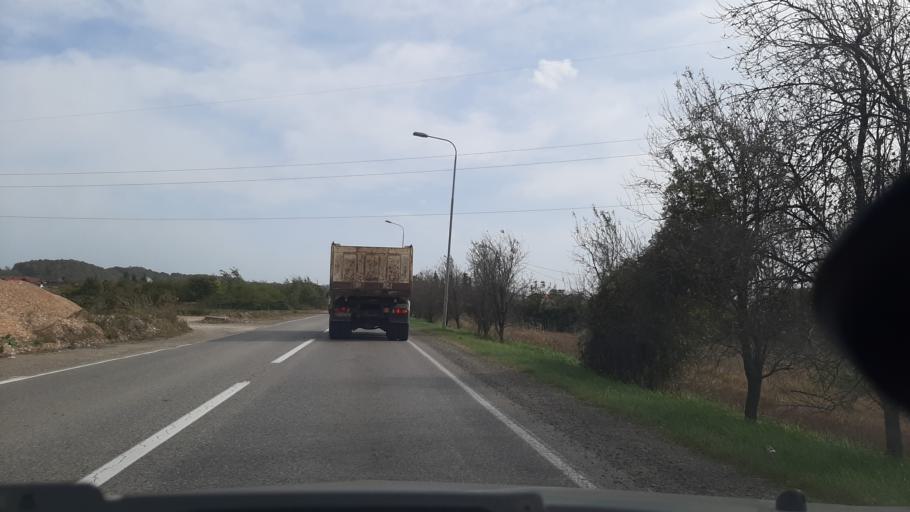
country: BA
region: Republika Srpska
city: Laktasi
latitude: 44.8778
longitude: 17.2943
